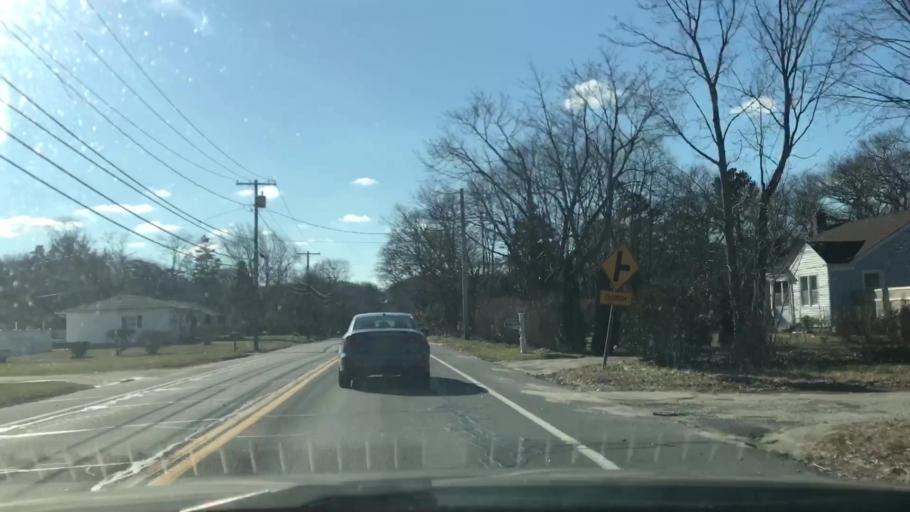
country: US
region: New York
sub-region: Suffolk County
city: Riverhead
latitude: 40.9434
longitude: -72.6567
